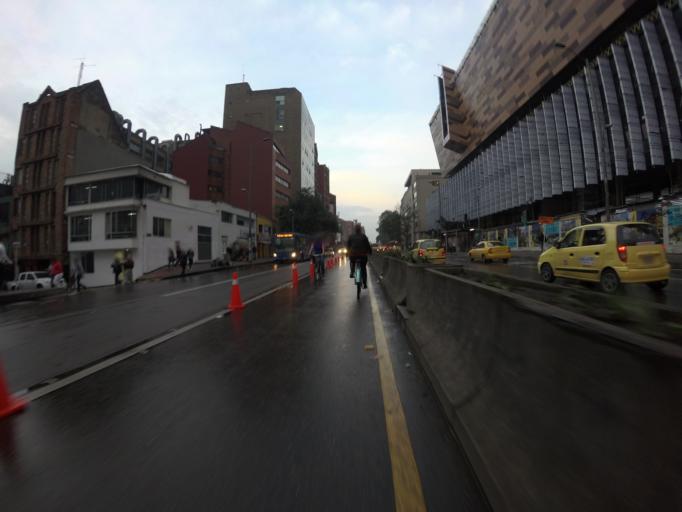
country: CO
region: Bogota D.C.
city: Bogota
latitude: 4.6274
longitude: -74.0655
